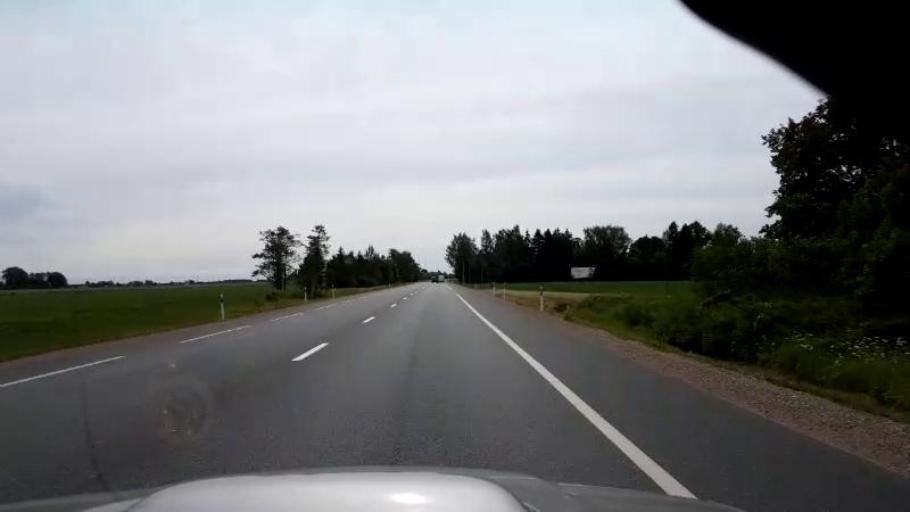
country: LV
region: Bauskas Rajons
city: Bauska
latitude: 56.4393
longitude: 24.1720
